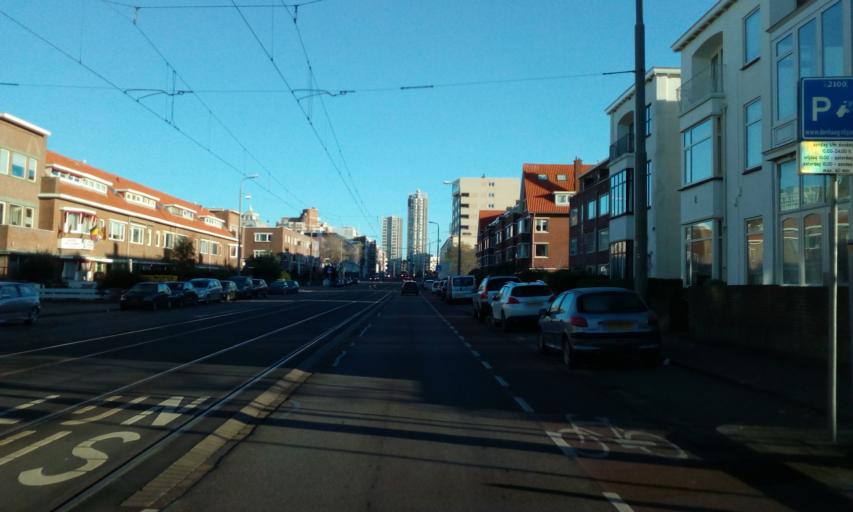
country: NL
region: South Holland
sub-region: Gemeente Den Haag
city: Scheveningen
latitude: 52.1095
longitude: 4.2785
